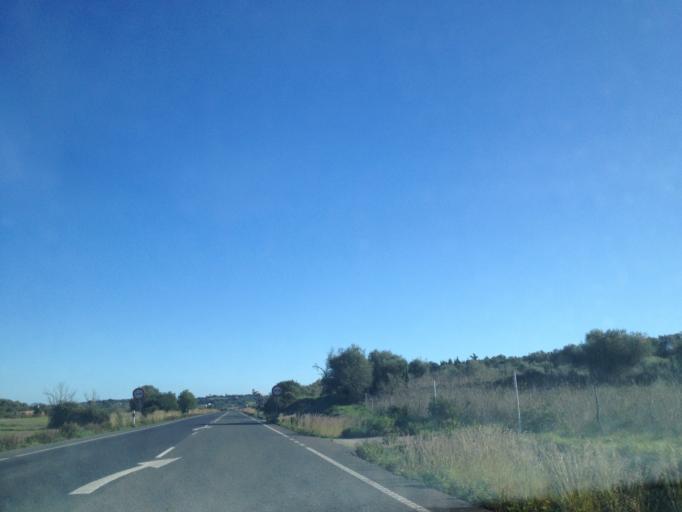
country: ES
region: Balearic Islands
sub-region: Illes Balears
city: Maria de la Salut
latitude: 39.6448
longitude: 3.0824
